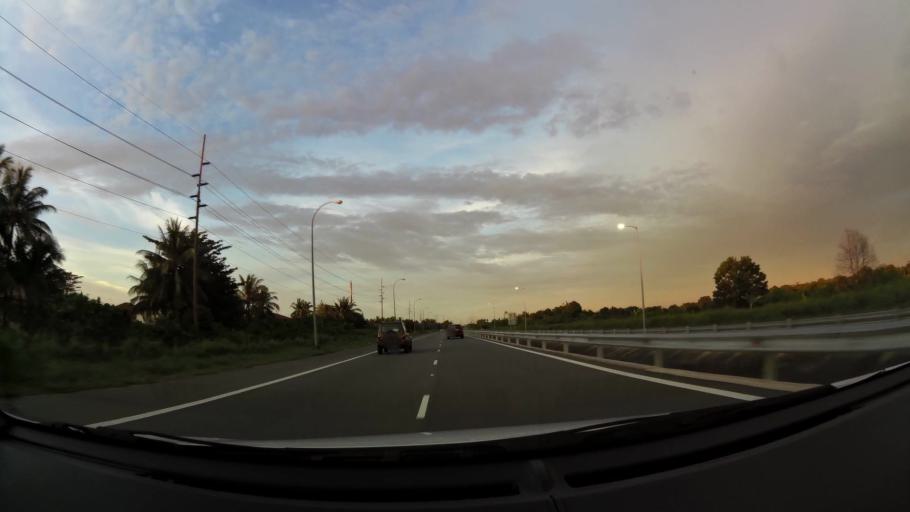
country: BN
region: Belait
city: Kuala Belait
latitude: 4.5736
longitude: 114.2287
